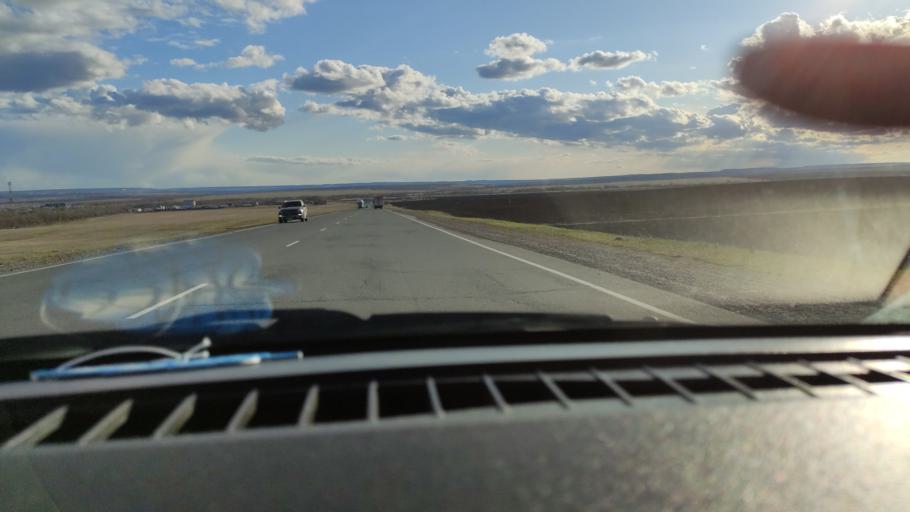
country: RU
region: Saratov
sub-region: Saratovskiy Rayon
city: Saratov
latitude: 51.7400
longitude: 46.0433
